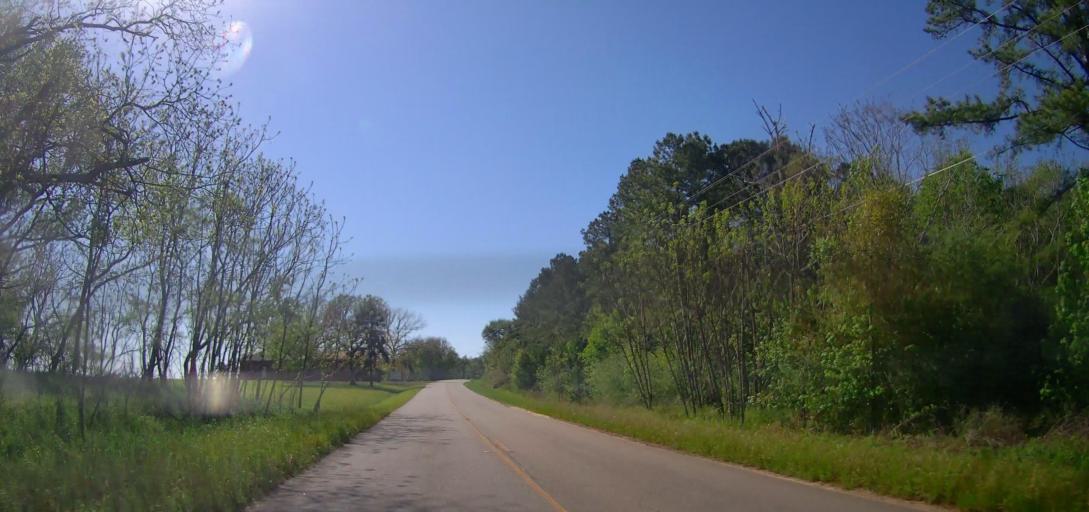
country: US
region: Georgia
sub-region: Pulaski County
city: Hawkinsville
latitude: 32.2407
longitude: -83.5604
